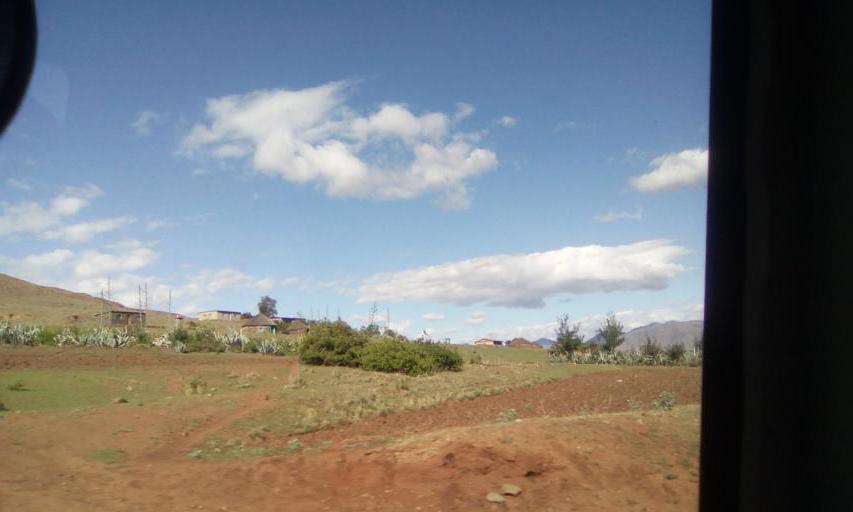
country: LS
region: Qacha's Nek
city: Qacha's Nek
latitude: -30.0484
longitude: 28.2836
